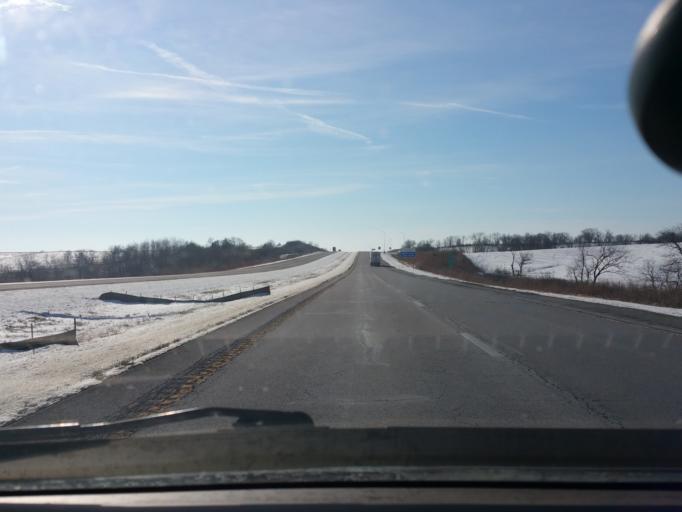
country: US
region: Iowa
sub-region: Decatur County
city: Lamoni
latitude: 40.5566
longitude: -93.9515
